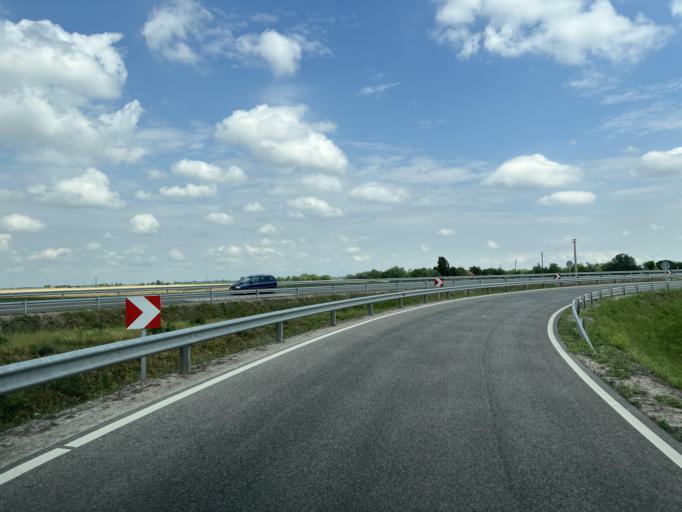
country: HU
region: Pest
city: Tortel
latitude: 47.1925
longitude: 19.9160
